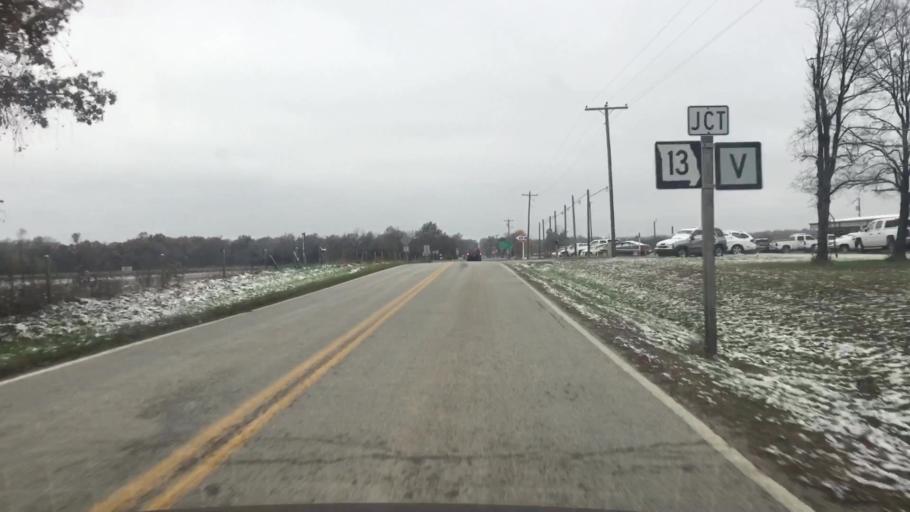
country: US
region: Missouri
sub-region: Saint Clair County
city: Osceola
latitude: 37.9899
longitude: -93.6487
